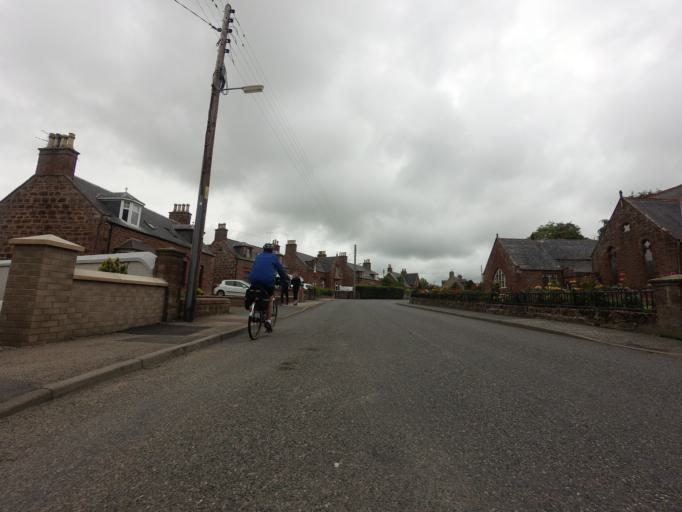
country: GB
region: Scotland
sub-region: Aberdeenshire
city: Turriff
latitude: 57.5374
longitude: -2.4541
